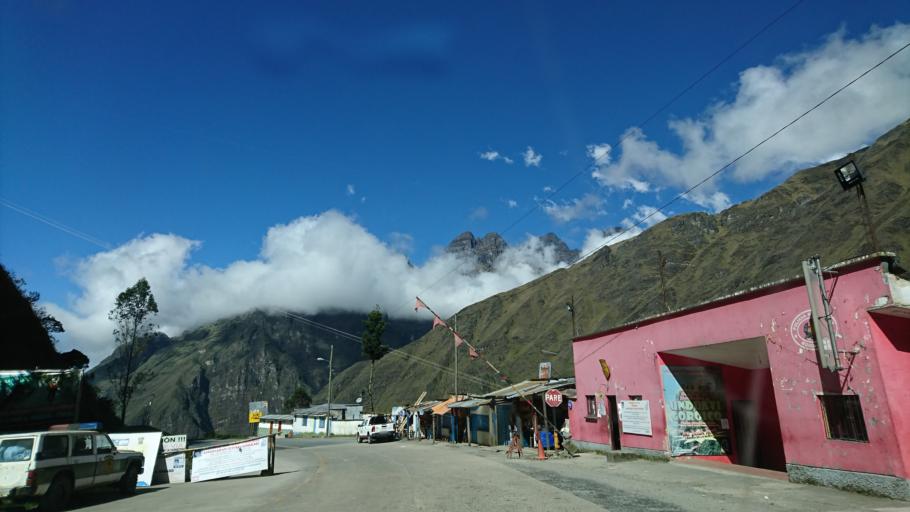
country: BO
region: La Paz
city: Coroico
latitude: -16.3108
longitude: -67.9096
